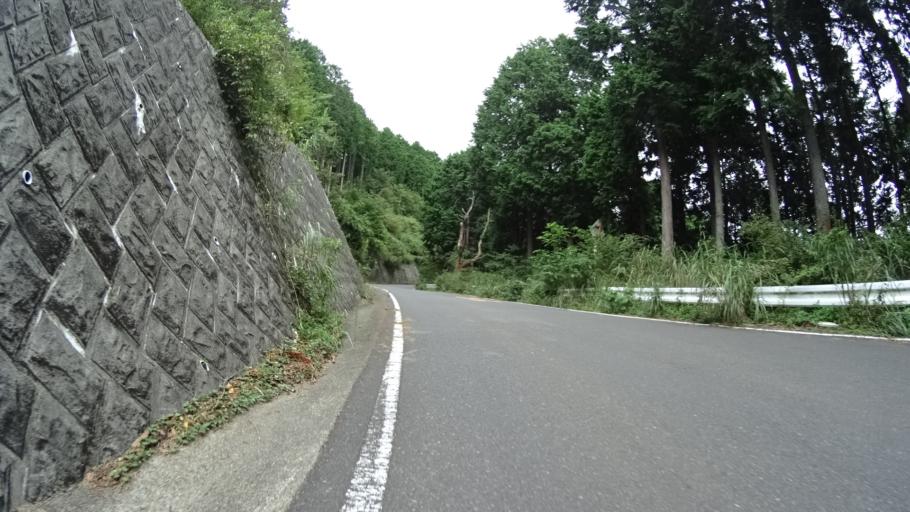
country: JP
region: Kanagawa
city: Hadano
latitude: 35.4132
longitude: 139.2130
